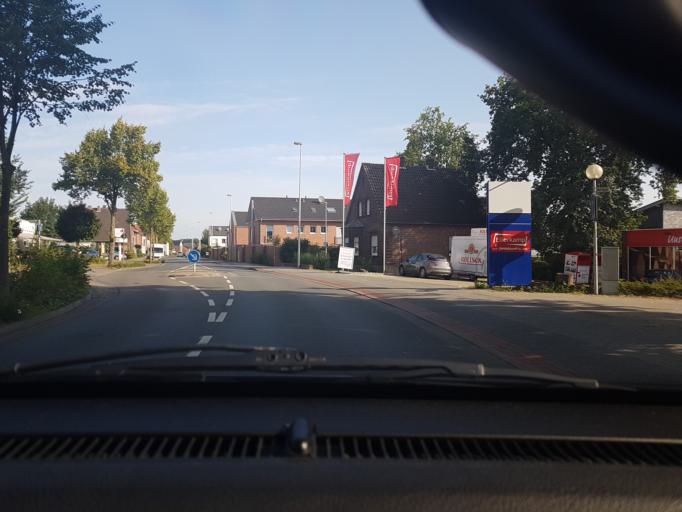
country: DE
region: North Rhine-Westphalia
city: Emsdetten
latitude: 52.1639
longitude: 7.5271
